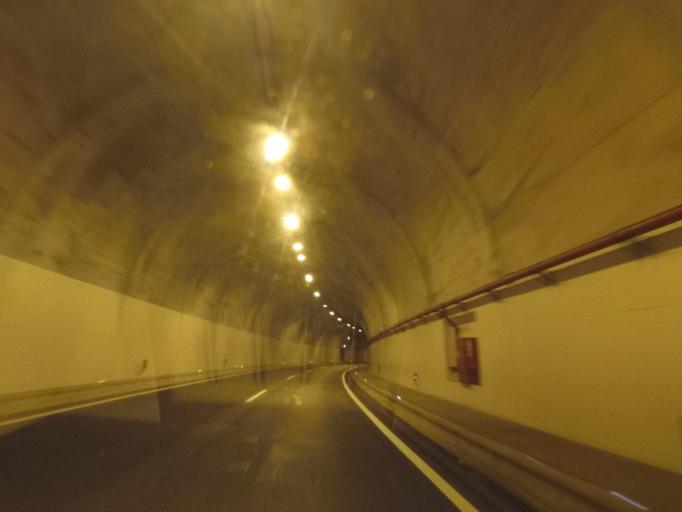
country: PT
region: Madeira
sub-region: Machico
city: Canical
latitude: 32.7454
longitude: -16.7428
